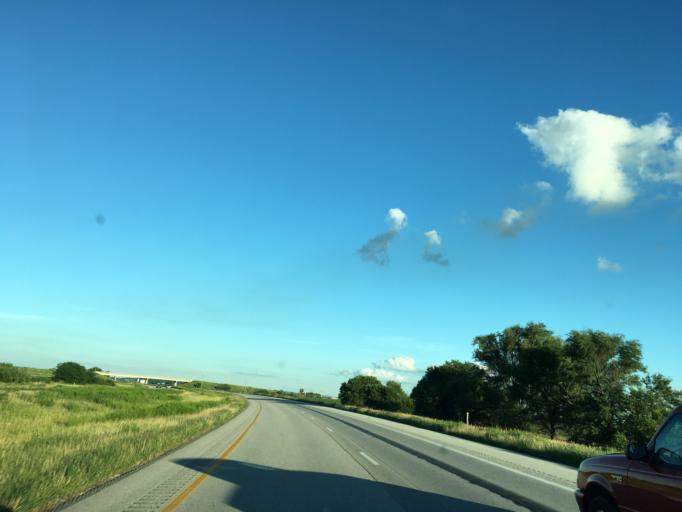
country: US
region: Iowa
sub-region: Fremont County
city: Hamburg
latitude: 40.6433
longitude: -95.7417
